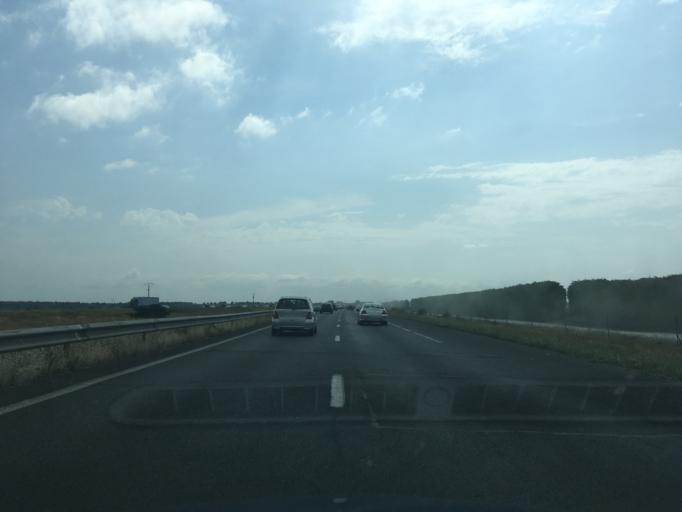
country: FR
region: Aquitaine
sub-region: Departement de la Gironde
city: Marcheprime
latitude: 44.6899
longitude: -0.7736
